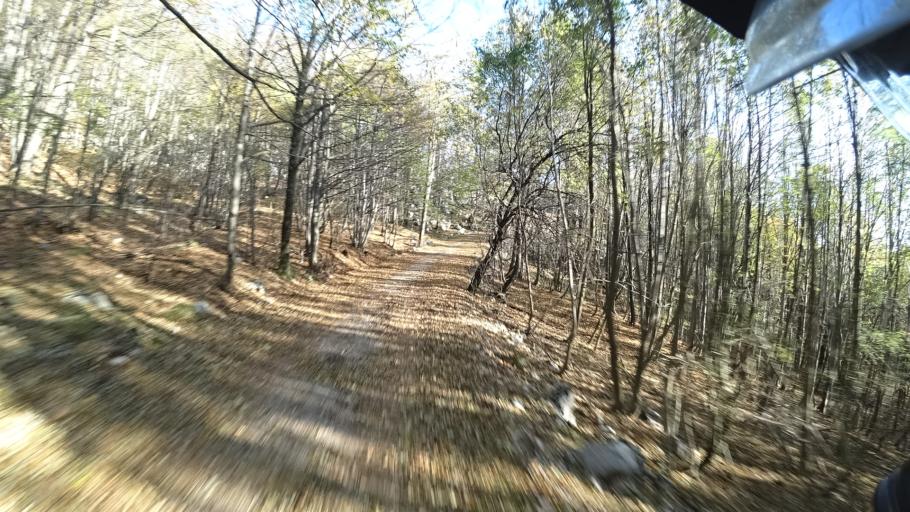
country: HR
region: Primorsko-Goranska
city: Klana
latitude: 45.4858
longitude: 14.4177
